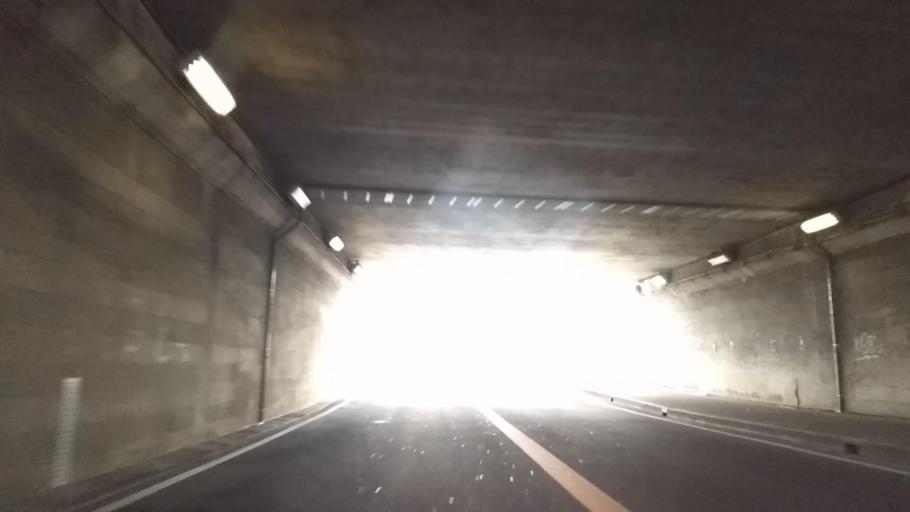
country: JP
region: Kanagawa
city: Hiratsuka
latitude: 35.3216
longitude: 139.3304
